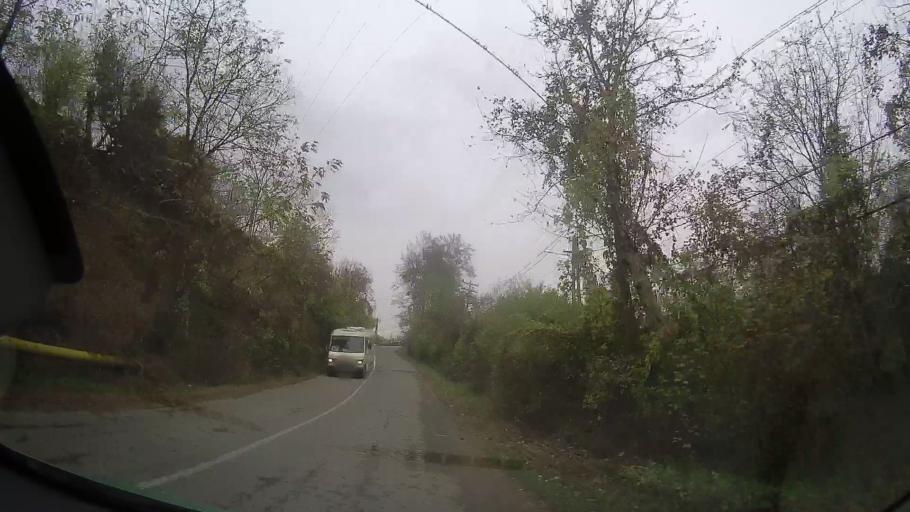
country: RO
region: Prahova
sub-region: Comuna Ceptura
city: Ceptura de Jos
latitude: 45.0320
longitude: 26.3199
